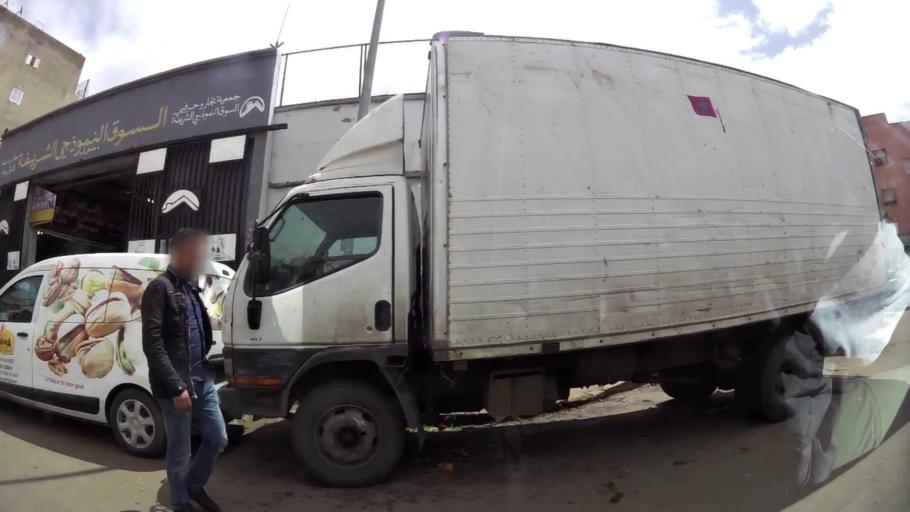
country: MA
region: Grand Casablanca
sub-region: Casablanca
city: Casablanca
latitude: 33.5361
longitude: -7.6025
